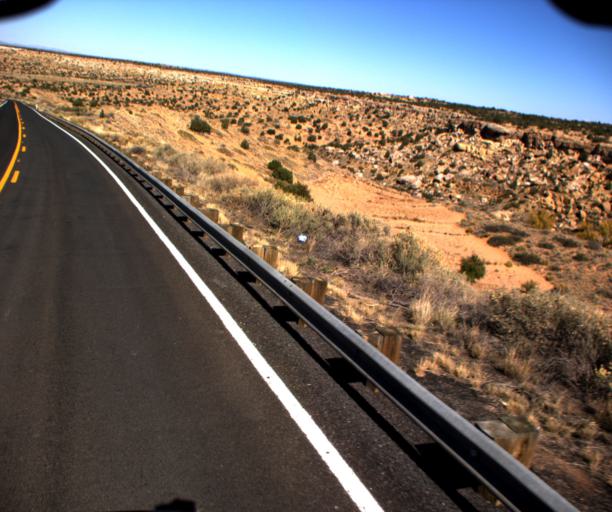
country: US
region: Arizona
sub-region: Navajo County
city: First Mesa
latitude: 35.9289
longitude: -110.6602
